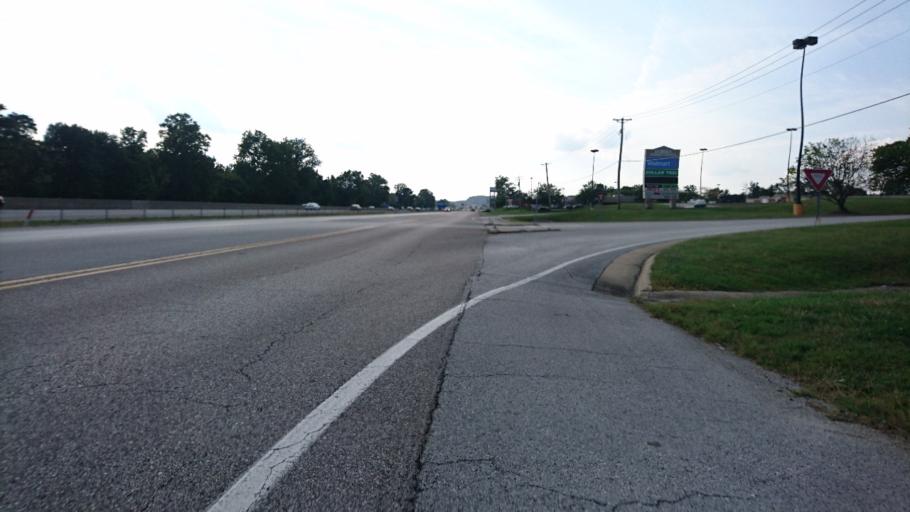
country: US
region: Missouri
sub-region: Saint Louis County
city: Eureka
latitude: 38.5045
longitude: -90.6554
